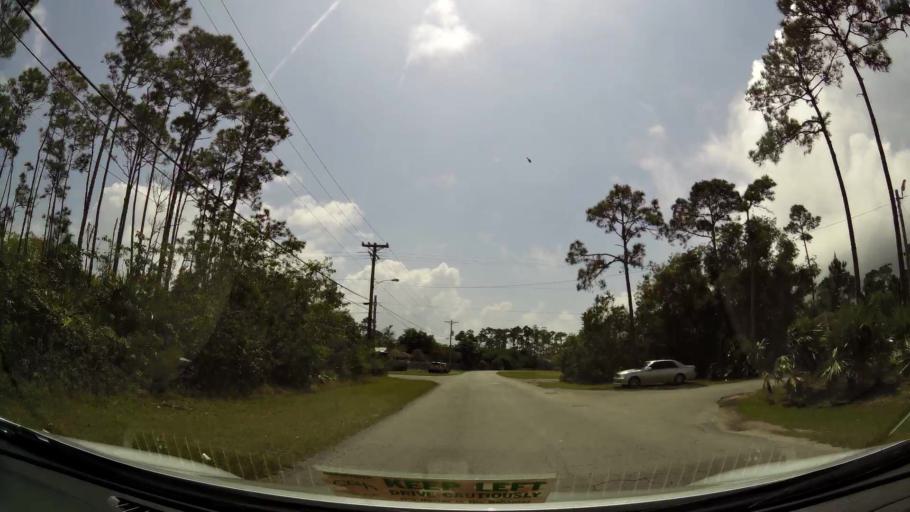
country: BS
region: Freeport
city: Lucaya
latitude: 26.5357
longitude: -78.6359
